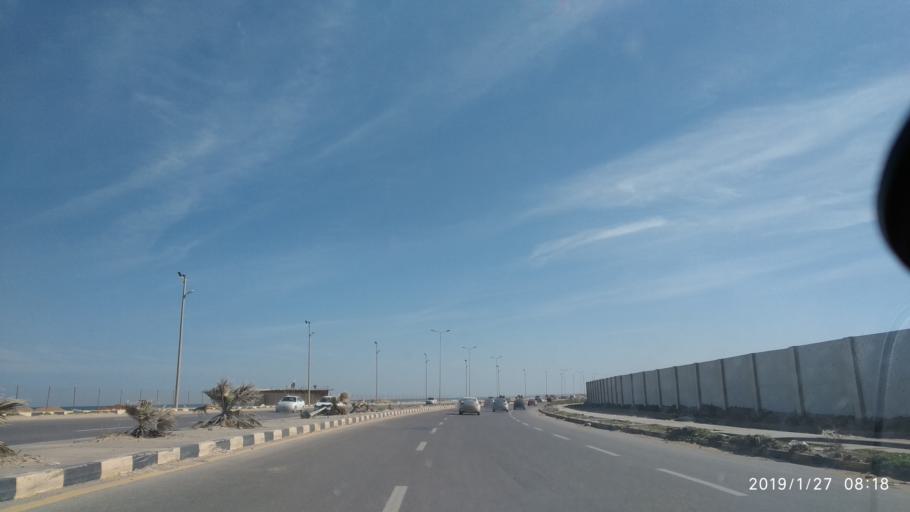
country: LY
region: Tripoli
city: Tagiura
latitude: 32.9088
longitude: 13.2877
